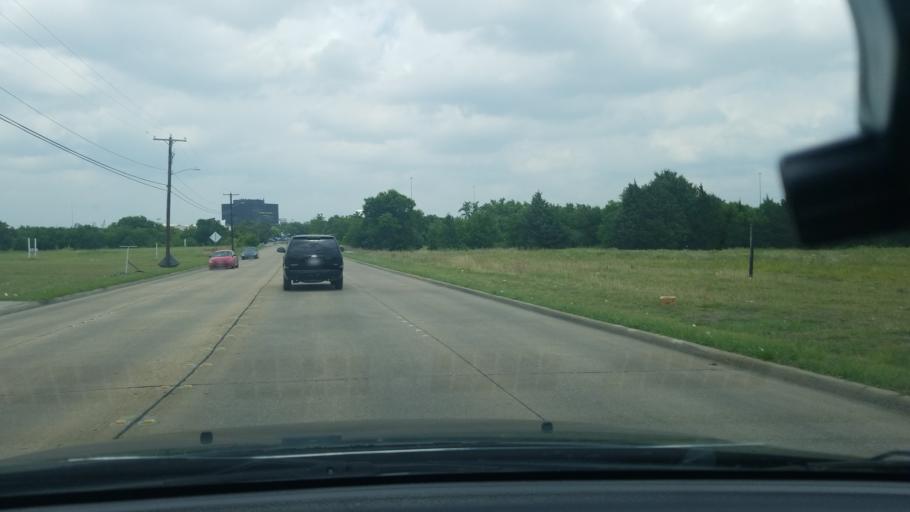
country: US
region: Texas
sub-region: Dallas County
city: Mesquite
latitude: 32.7991
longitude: -96.6327
